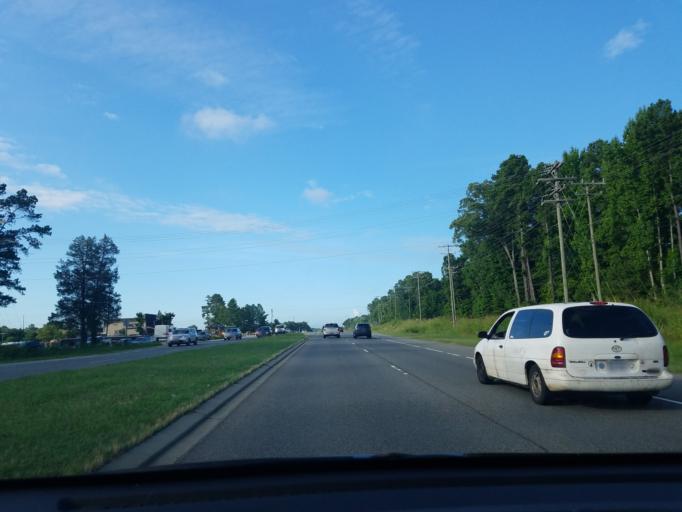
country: US
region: North Carolina
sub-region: Wake County
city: Morrisville
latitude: 35.8714
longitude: -78.8917
